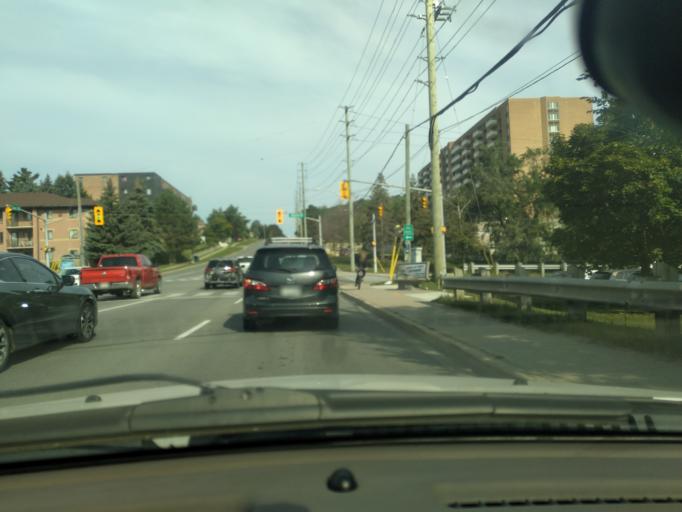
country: CA
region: Ontario
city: Barrie
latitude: 44.3868
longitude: -79.7088
